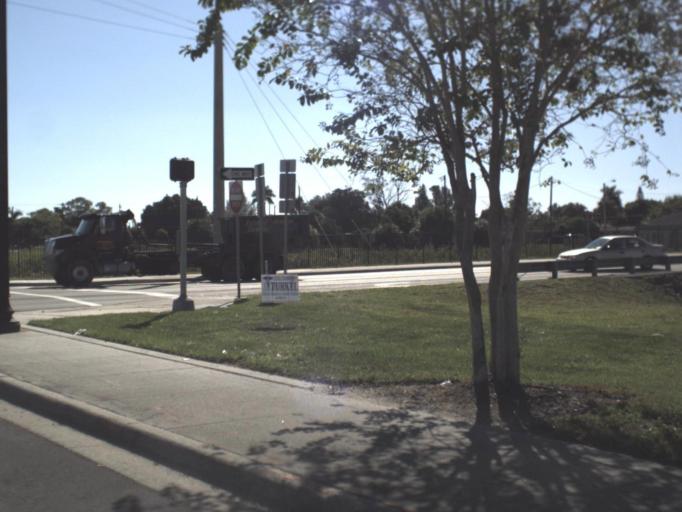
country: US
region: Florida
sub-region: Lee County
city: Fort Myers
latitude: 26.6410
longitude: -81.8402
